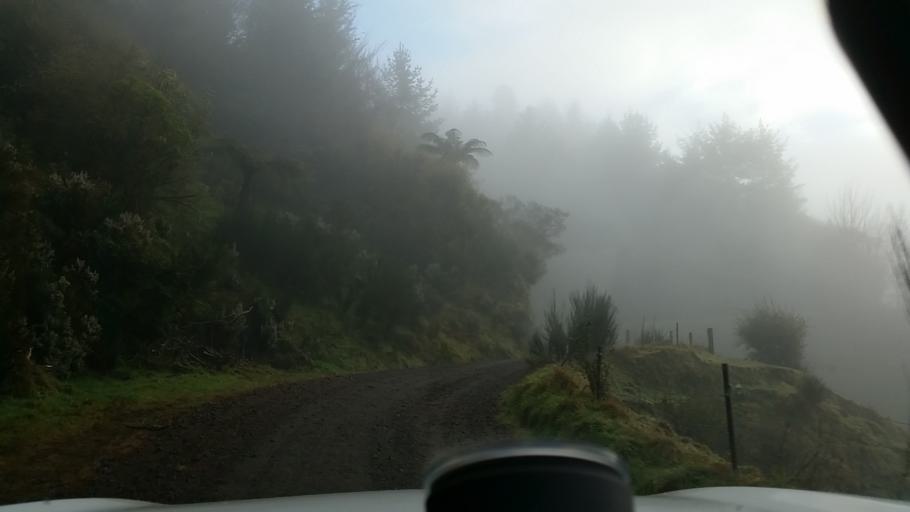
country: NZ
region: Taranaki
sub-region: South Taranaki District
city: Eltham
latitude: -39.4136
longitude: 174.4297
